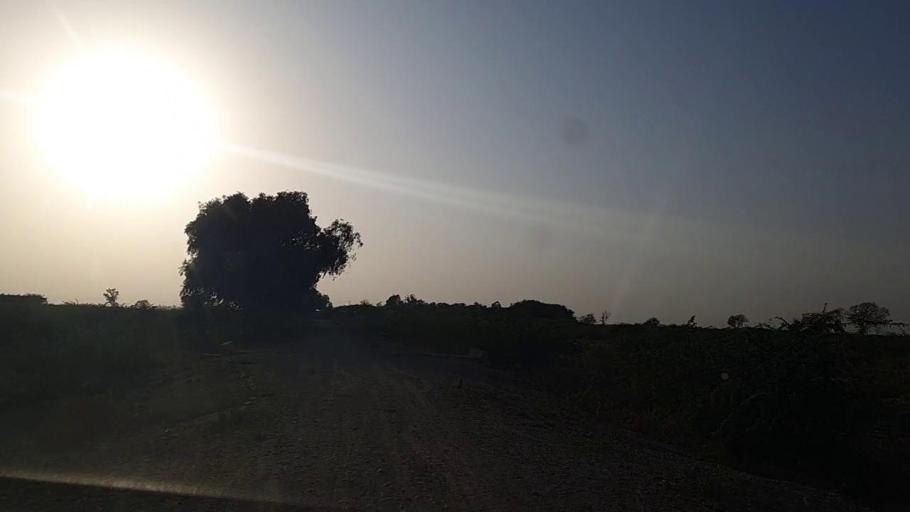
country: PK
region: Sindh
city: Naukot
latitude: 24.6432
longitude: 69.2559
